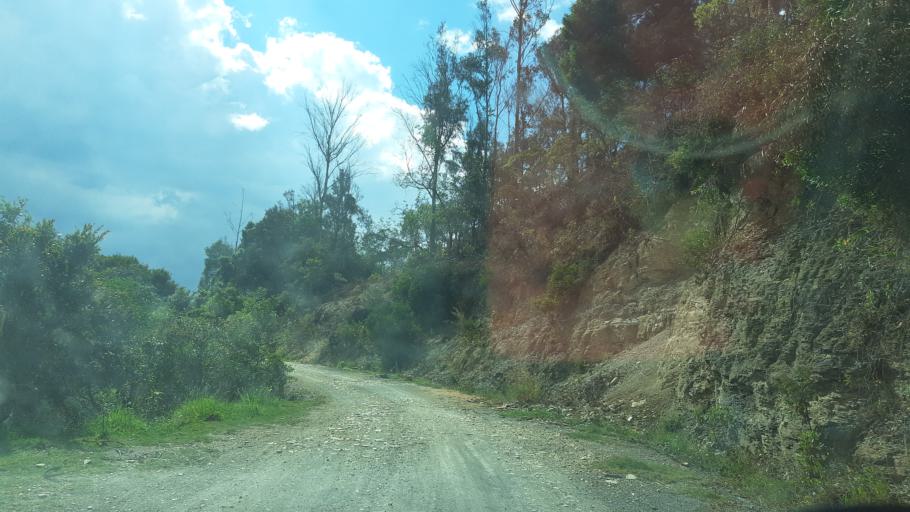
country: CO
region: Boyaca
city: Santa Sofia
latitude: 5.7267
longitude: -73.5480
